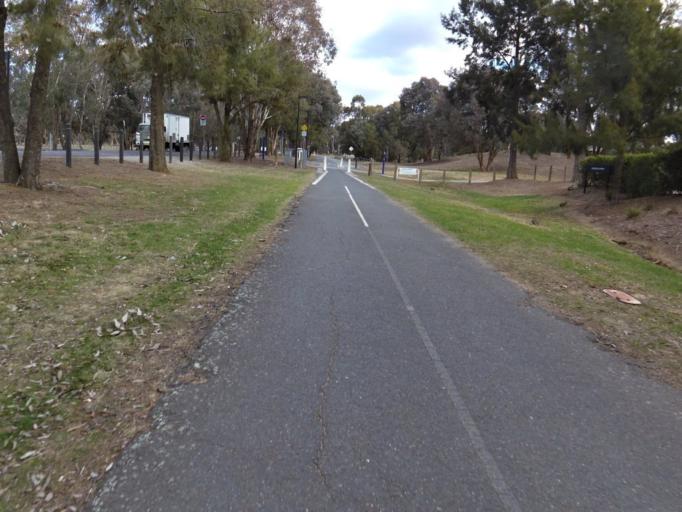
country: AU
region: Australian Capital Territory
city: Kaleen
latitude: -35.2488
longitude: 149.1051
